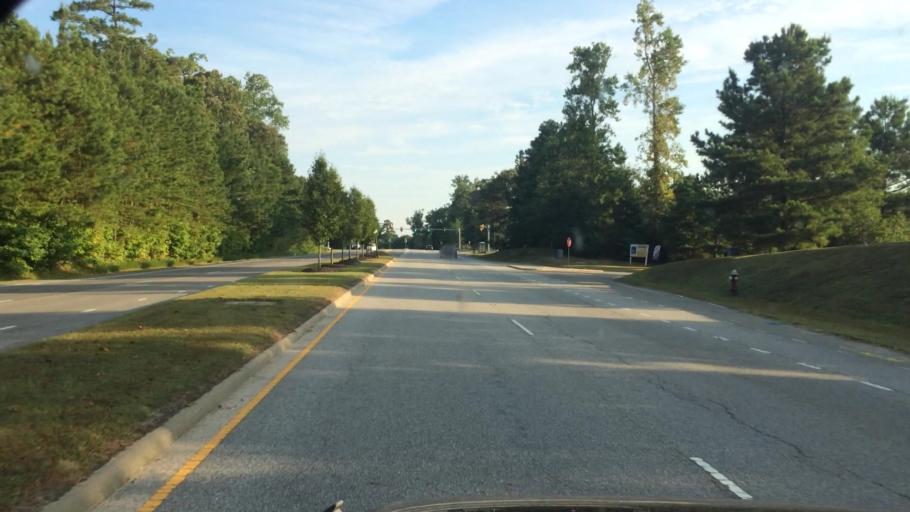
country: US
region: Virginia
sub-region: James City County
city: Williamsburg
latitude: 37.3374
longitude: -76.7375
